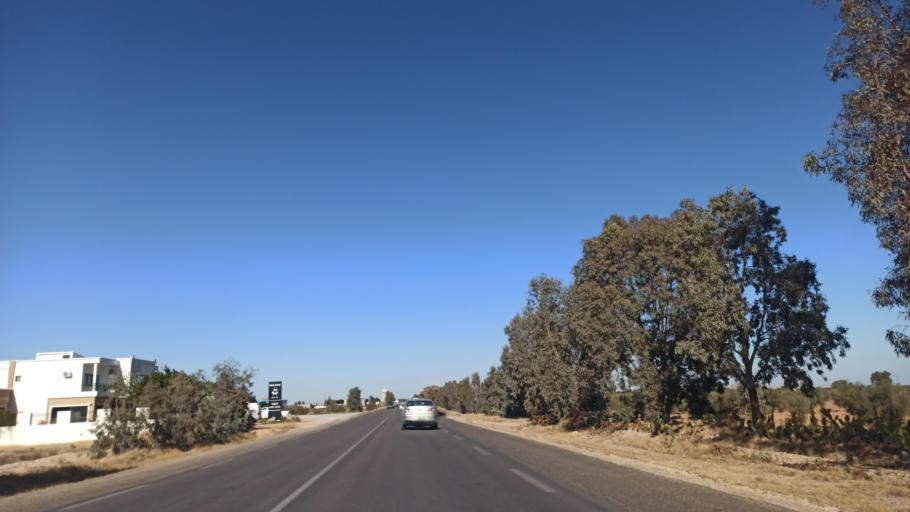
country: TN
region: Sidi Bu Zayd
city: Jilma
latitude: 35.1414
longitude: 9.3617
